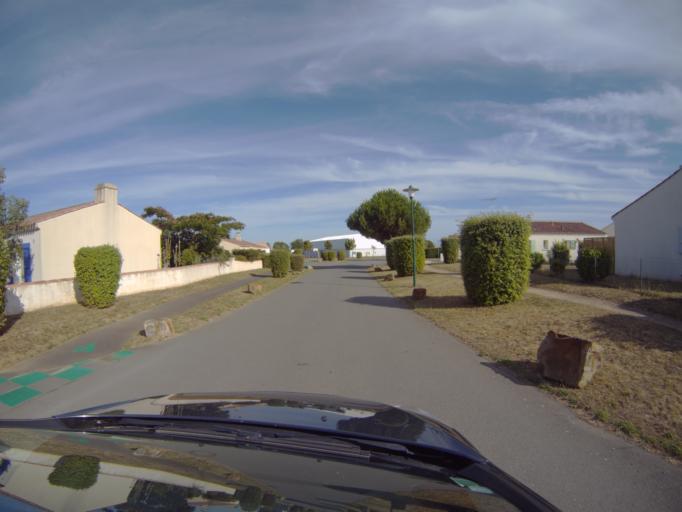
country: FR
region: Pays de la Loire
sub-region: Departement de la Vendee
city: Angles
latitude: 46.4092
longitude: -1.3953
